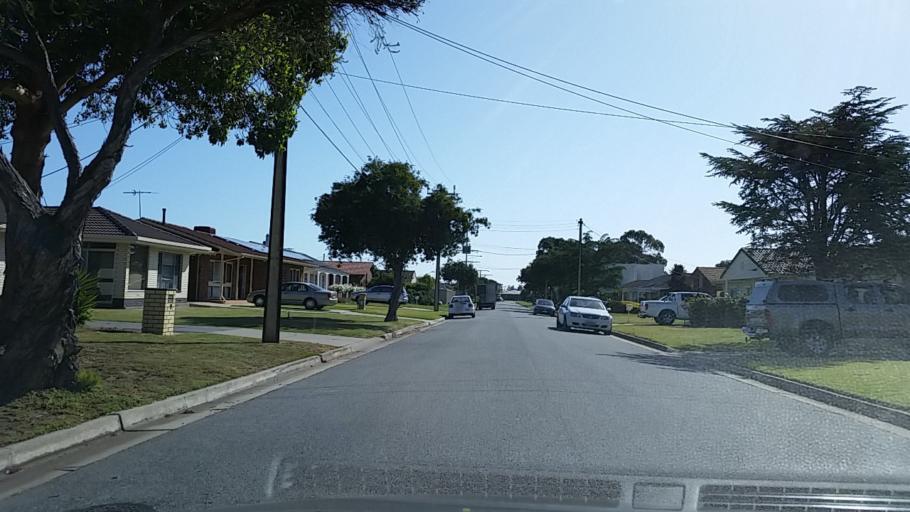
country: AU
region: South Australia
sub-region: Charles Sturt
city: Henley Beach
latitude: -34.9187
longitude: 138.5120
